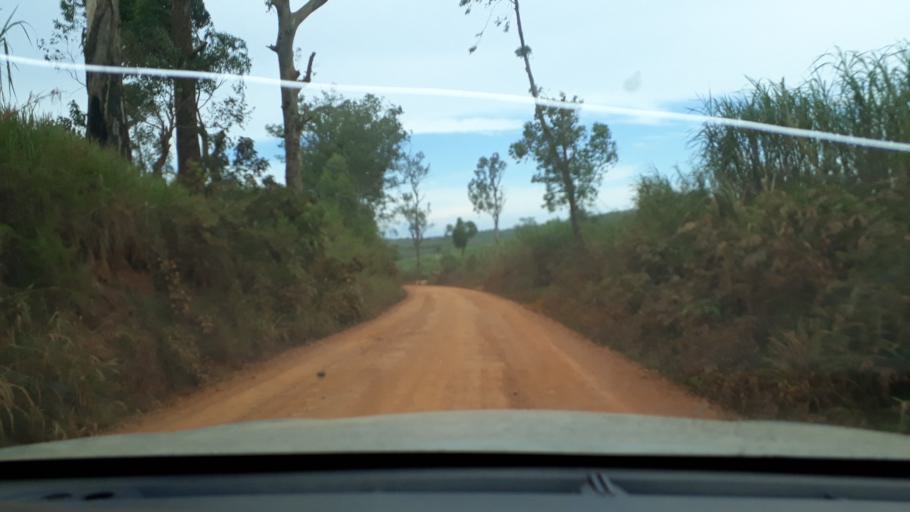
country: CD
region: Eastern Province
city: Bunia
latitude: 1.8668
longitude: 30.4797
